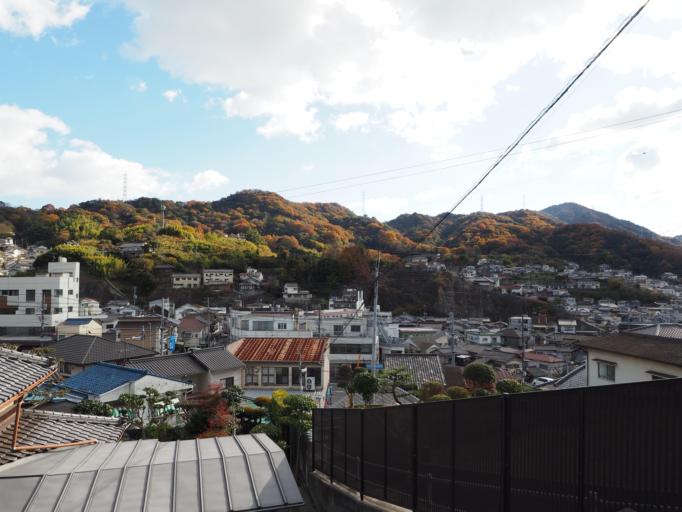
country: JP
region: Hiroshima
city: Kure
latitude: 34.2537
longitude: 132.5826
